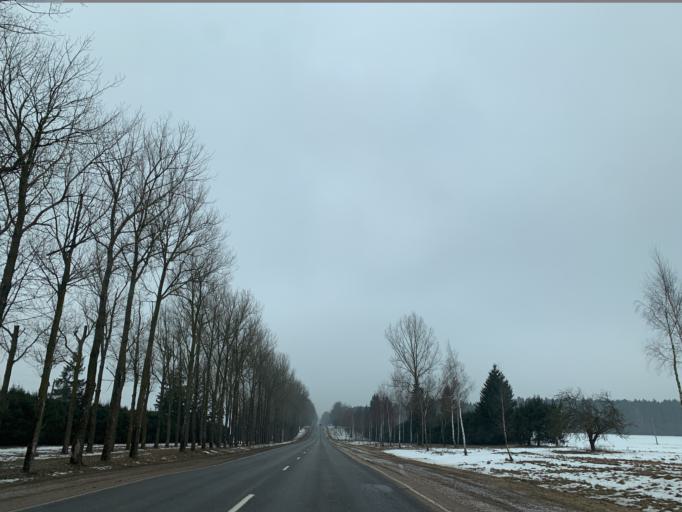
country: BY
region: Minsk
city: Haradzyeya
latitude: 53.3447
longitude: 26.5190
